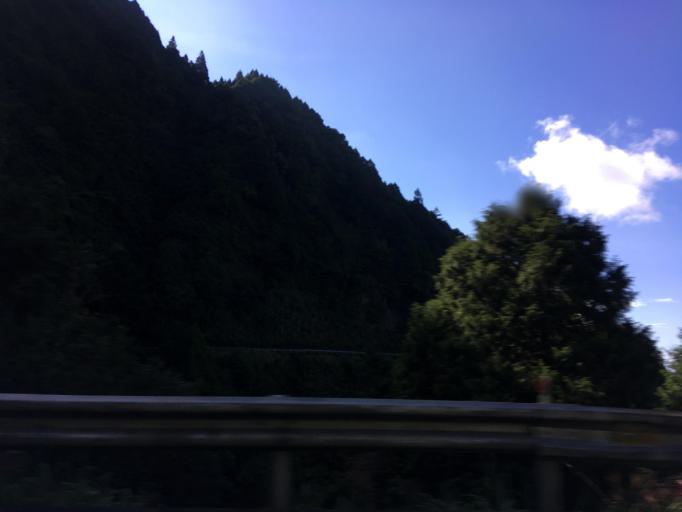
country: TW
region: Taiwan
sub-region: Yilan
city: Yilan
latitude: 24.5041
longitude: 121.5585
